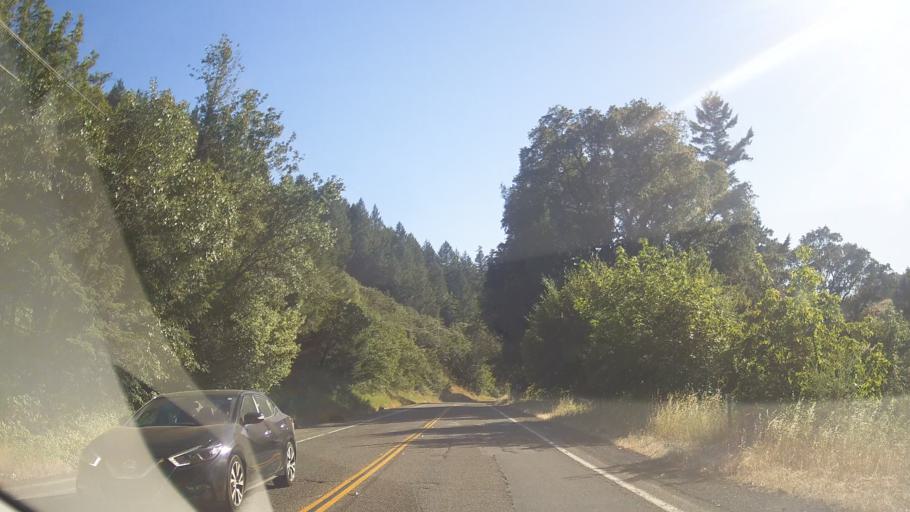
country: US
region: California
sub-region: Mendocino County
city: Willits
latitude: 39.4070
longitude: -123.3810
